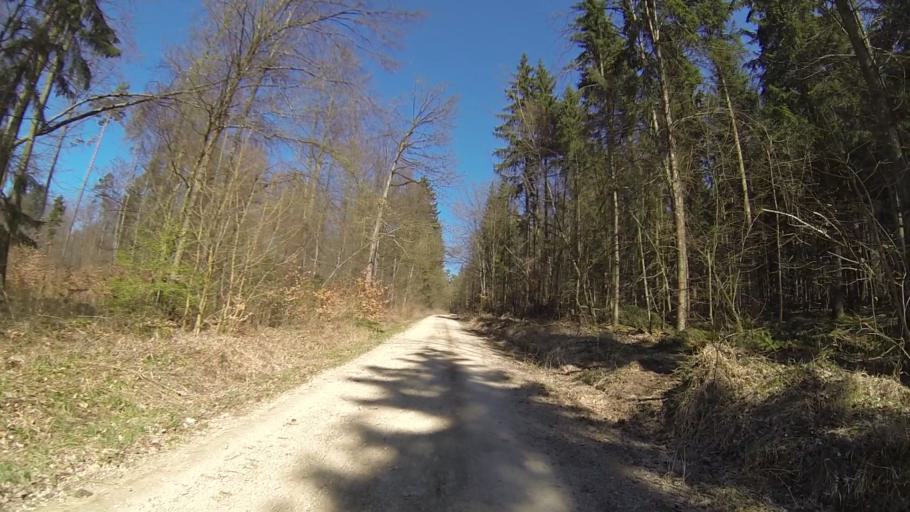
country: DE
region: Baden-Wuerttemberg
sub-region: Regierungsbezirk Stuttgart
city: Nattheim
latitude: 48.6799
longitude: 10.2726
